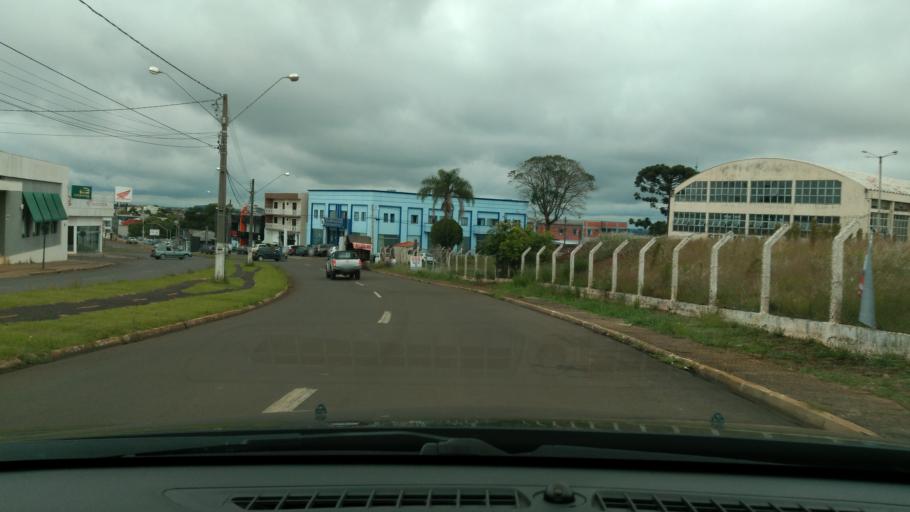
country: BR
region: Parana
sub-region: Guarapuava
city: Guarapuava
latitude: -25.3829
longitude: -51.4687
